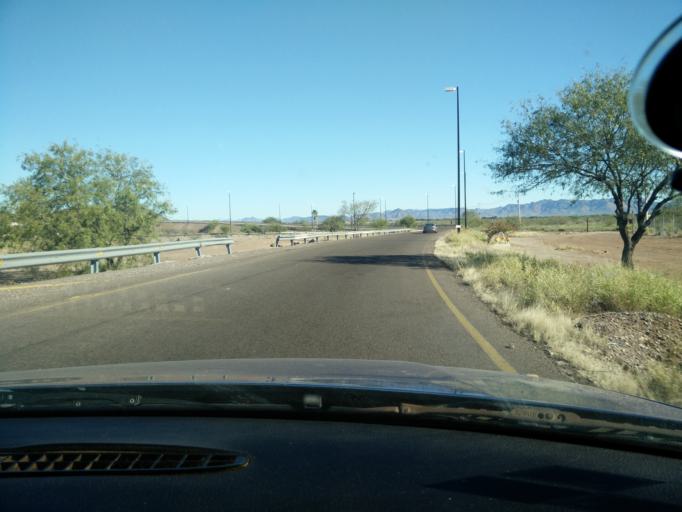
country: MX
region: Sonora
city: Heroica Guaymas
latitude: 27.9840
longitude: -110.9398
